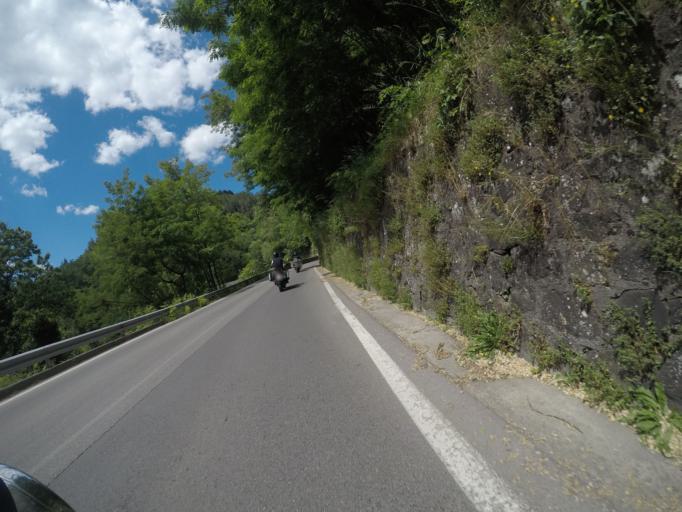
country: IT
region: Tuscany
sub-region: Provincia di Lucca
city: San Romano in Garfagnana
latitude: 44.1676
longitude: 10.3516
